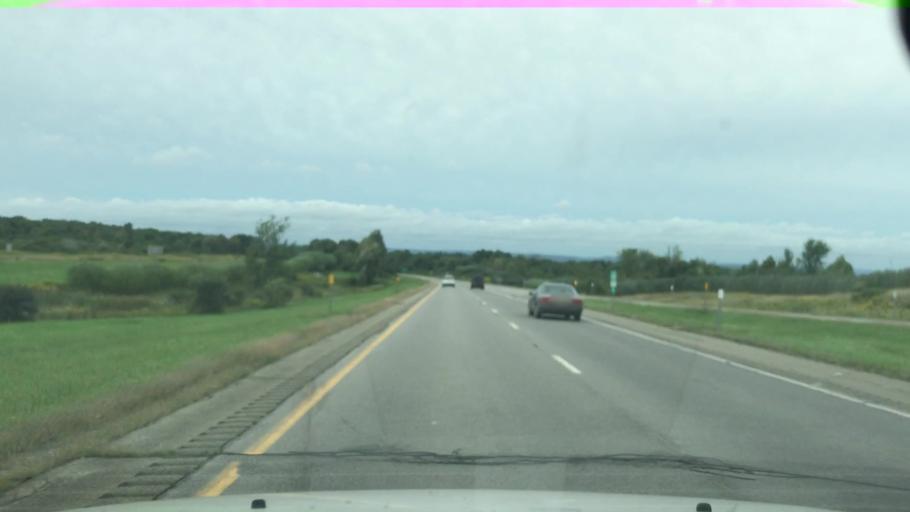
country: US
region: New York
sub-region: Erie County
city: Springville
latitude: 42.5502
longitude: -78.7115
